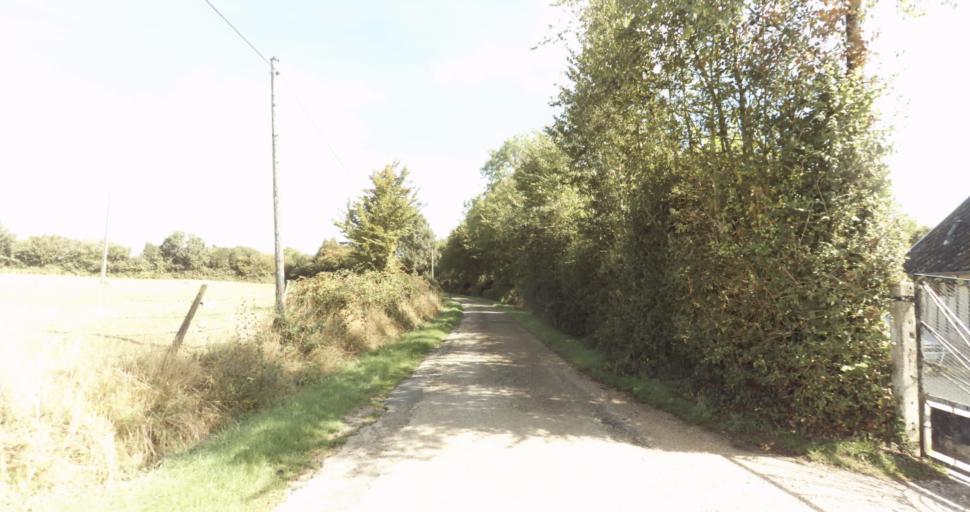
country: FR
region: Lower Normandy
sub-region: Departement du Calvados
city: Orbec
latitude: 48.9357
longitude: 0.3915
